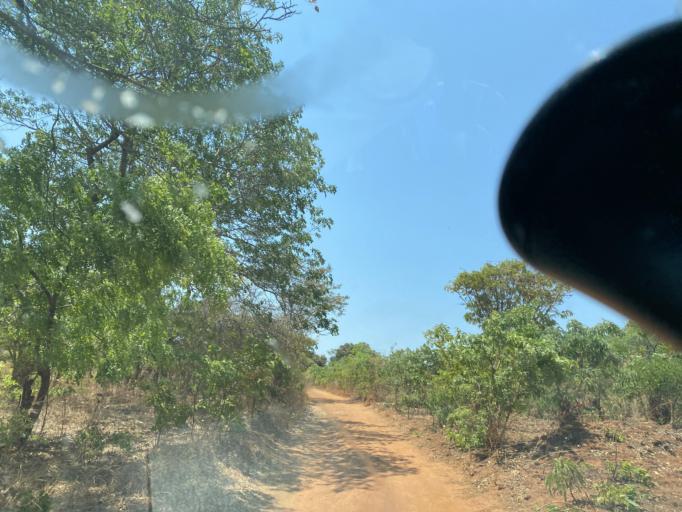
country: ZM
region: Lusaka
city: Chongwe
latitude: -15.4235
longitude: 29.1794
